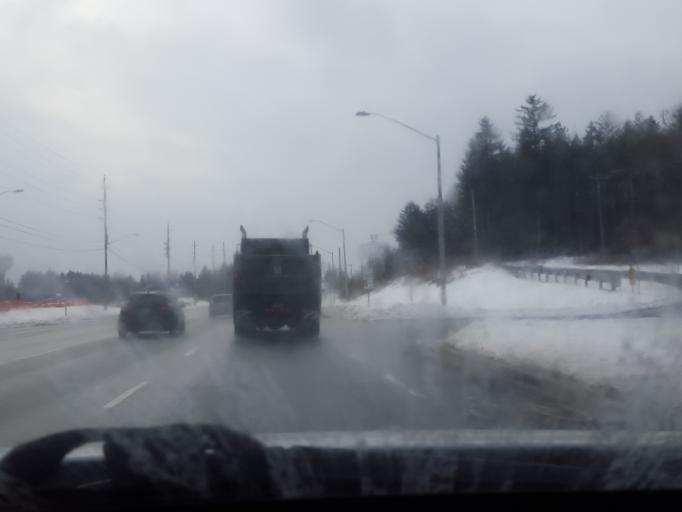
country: CA
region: Ontario
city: Newmarket
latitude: 43.9641
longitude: -79.4535
